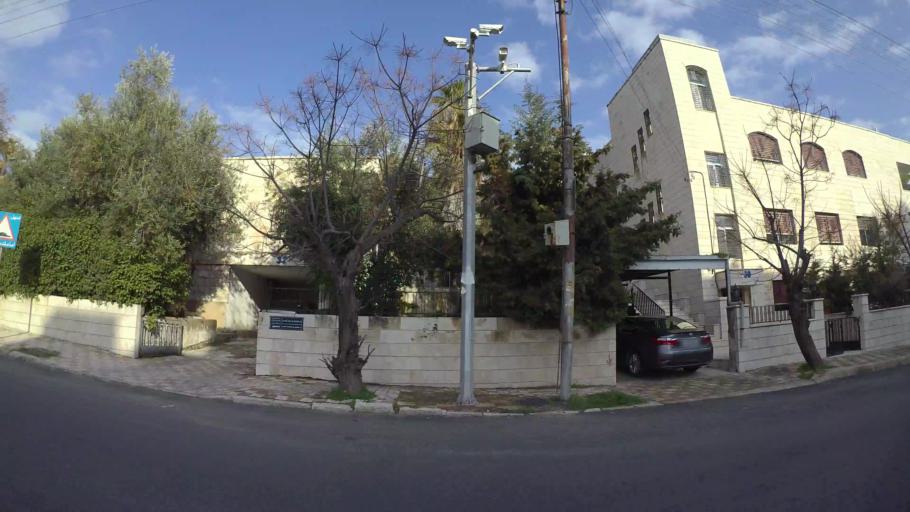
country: JO
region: Amman
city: Al Jubayhah
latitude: 31.9841
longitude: 35.8756
